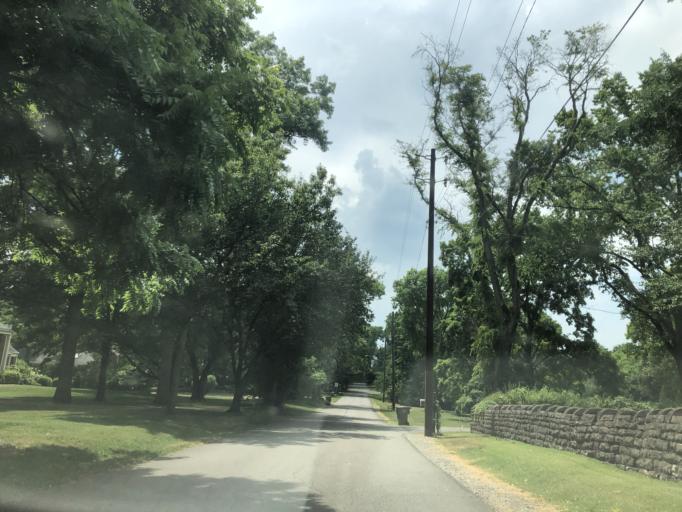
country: US
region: Tennessee
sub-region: Davidson County
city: Oak Hill
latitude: 36.1187
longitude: -86.8169
